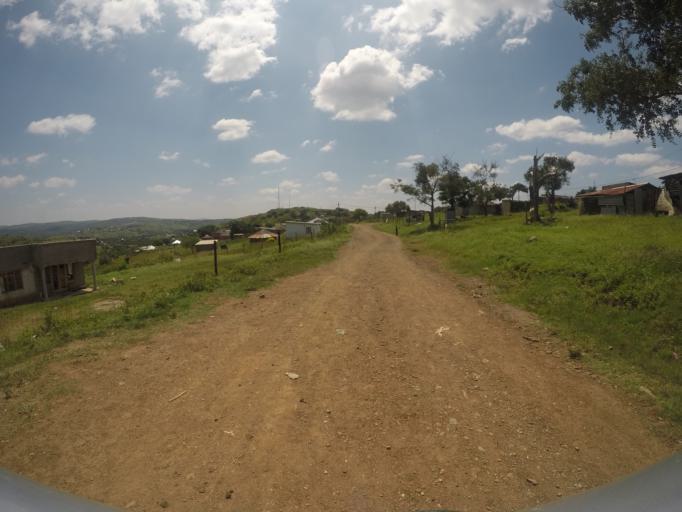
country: ZA
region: KwaZulu-Natal
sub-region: uThungulu District Municipality
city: Empangeni
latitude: -28.6046
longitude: 31.7407
